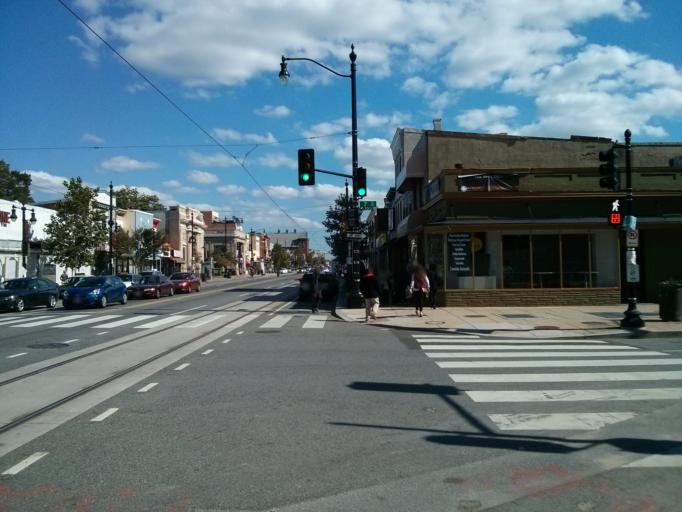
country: US
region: Washington, D.C.
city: Washington, D.C.
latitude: 38.9001
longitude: -76.9963
